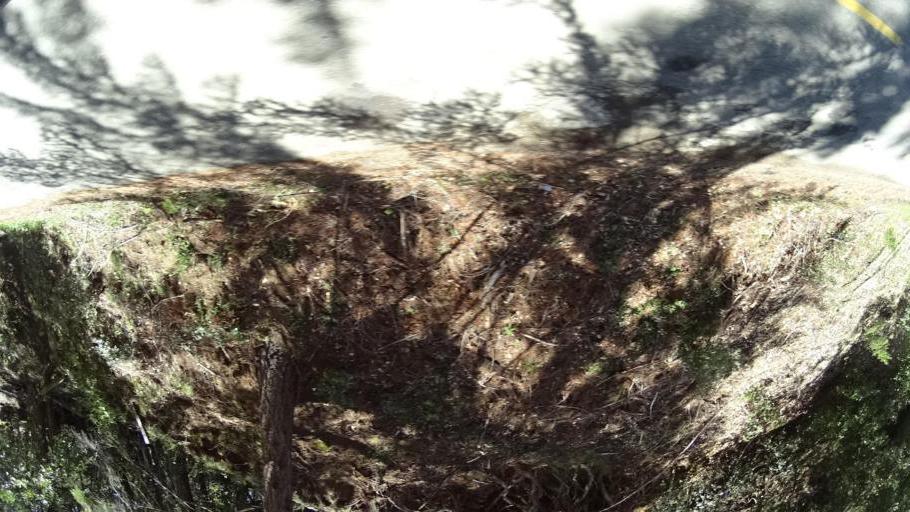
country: US
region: California
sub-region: Humboldt County
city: Rio Dell
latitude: 40.2870
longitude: -124.0554
